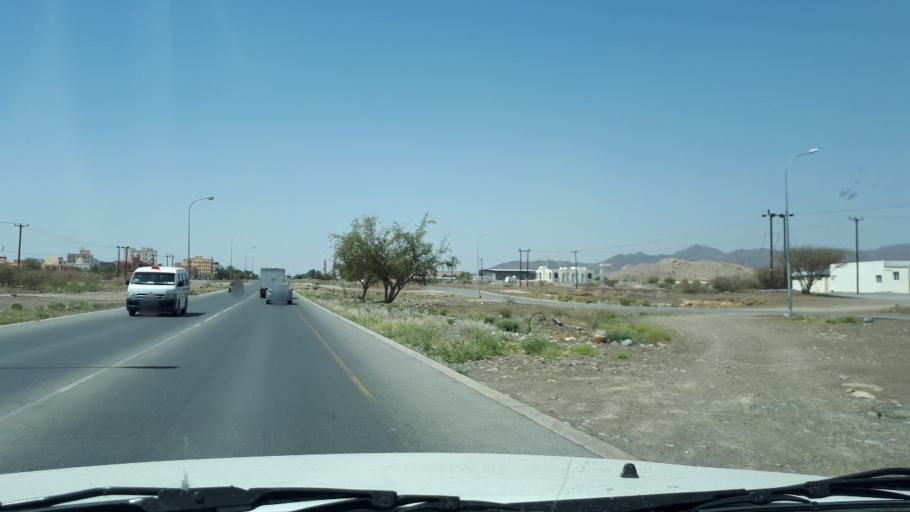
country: OM
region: Muhafazat ad Dakhiliyah
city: Bahla'
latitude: 23.0055
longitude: 57.3211
